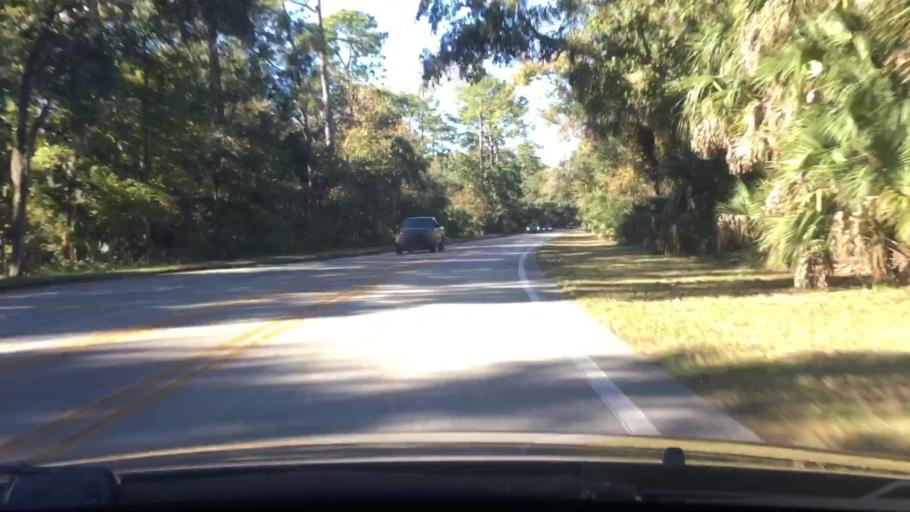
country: US
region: Florida
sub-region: Volusia County
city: Ormond-by-the-Sea
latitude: 29.3598
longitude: -81.1208
